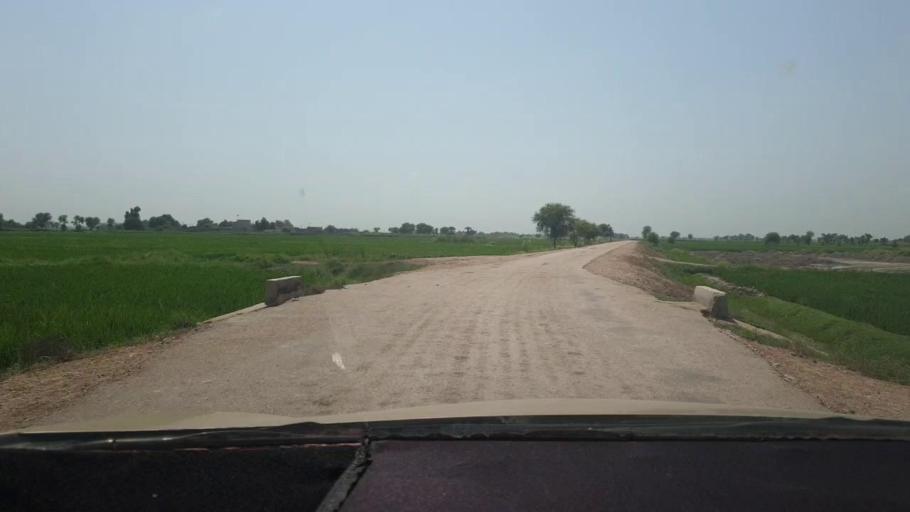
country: PK
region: Sindh
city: Miro Khan
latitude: 27.6667
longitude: 68.0960
